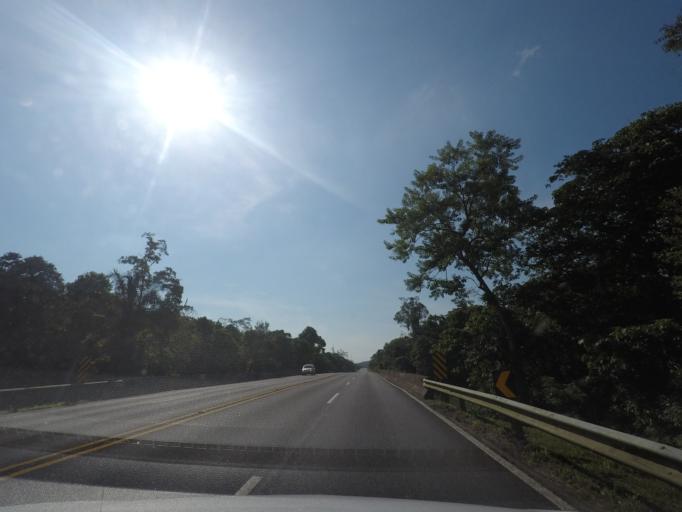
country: BR
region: Parana
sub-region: Paranagua
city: Paranagua
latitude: -25.5901
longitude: -48.6113
